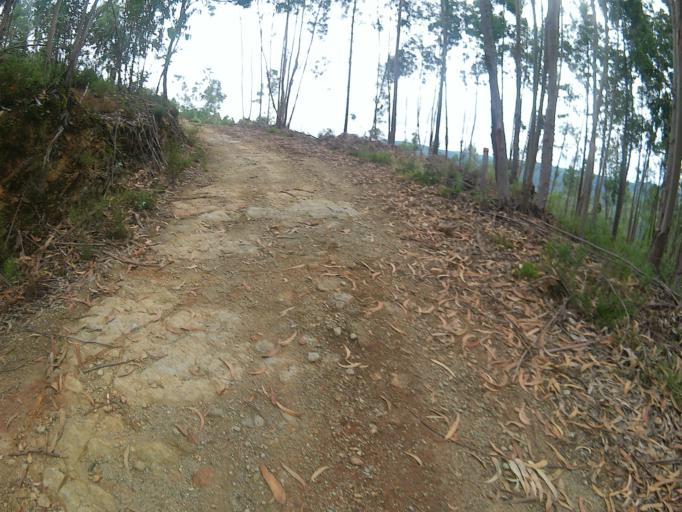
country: PT
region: Aveiro
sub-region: Albergaria-A-Velha
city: Branca
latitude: 40.7588
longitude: -8.4298
